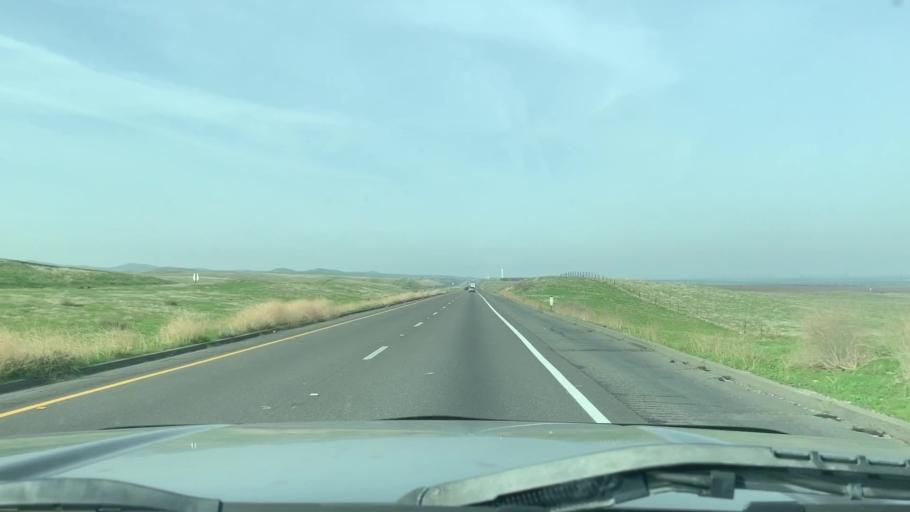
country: US
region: California
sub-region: Kings County
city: Kettleman City
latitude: 36.0308
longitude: -120.0227
